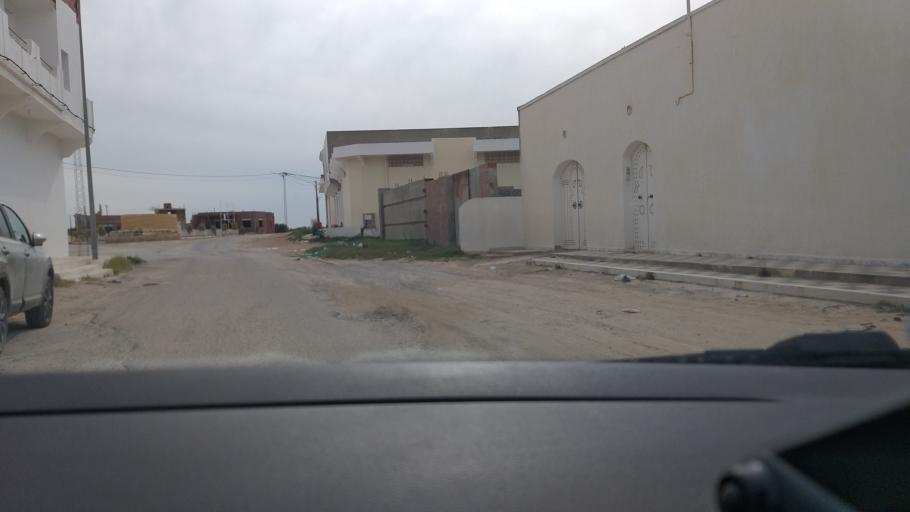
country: TN
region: Al Mahdiyah
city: El Jem
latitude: 35.2839
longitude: 10.7122
